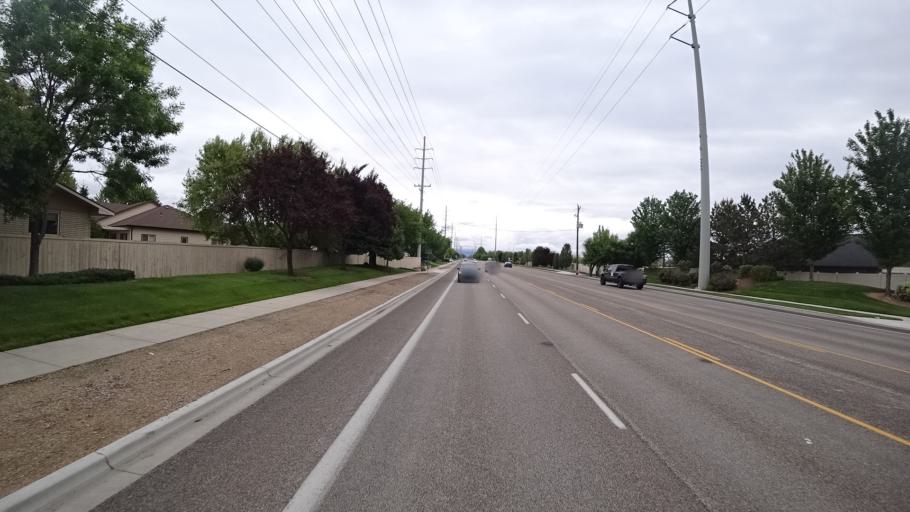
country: US
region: Idaho
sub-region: Ada County
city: Meridian
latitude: 43.6481
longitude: -116.3651
